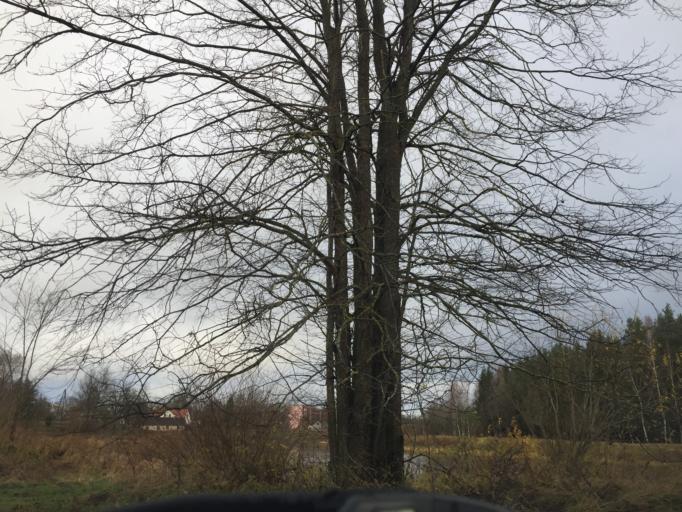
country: LV
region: Valmieras Rajons
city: Valmiera
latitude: 57.5316
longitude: 25.4341
